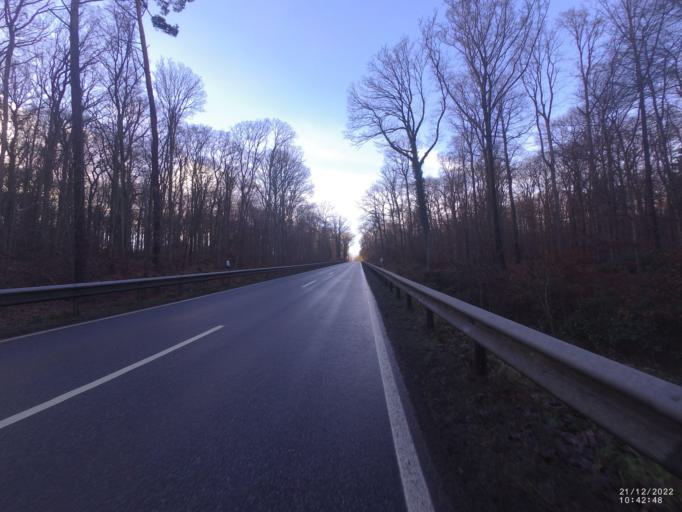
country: DE
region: Rheinland-Pfalz
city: Konigsfeld
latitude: 50.5024
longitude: 7.1933
